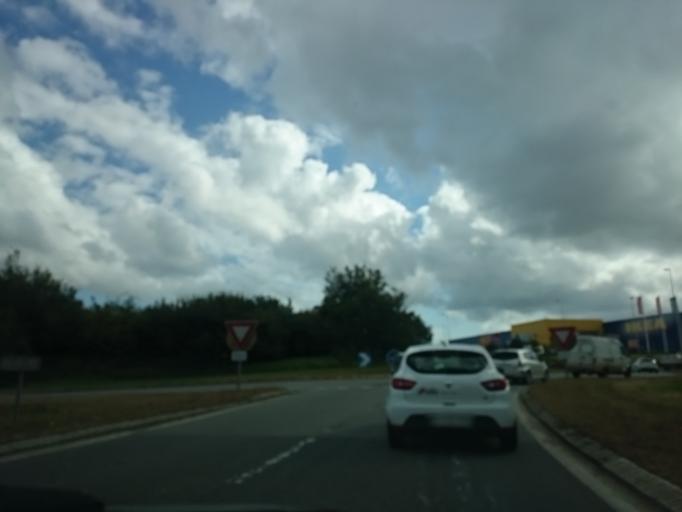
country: FR
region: Brittany
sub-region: Departement du Finistere
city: Gouesnou
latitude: 48.4194
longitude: -4.4391
